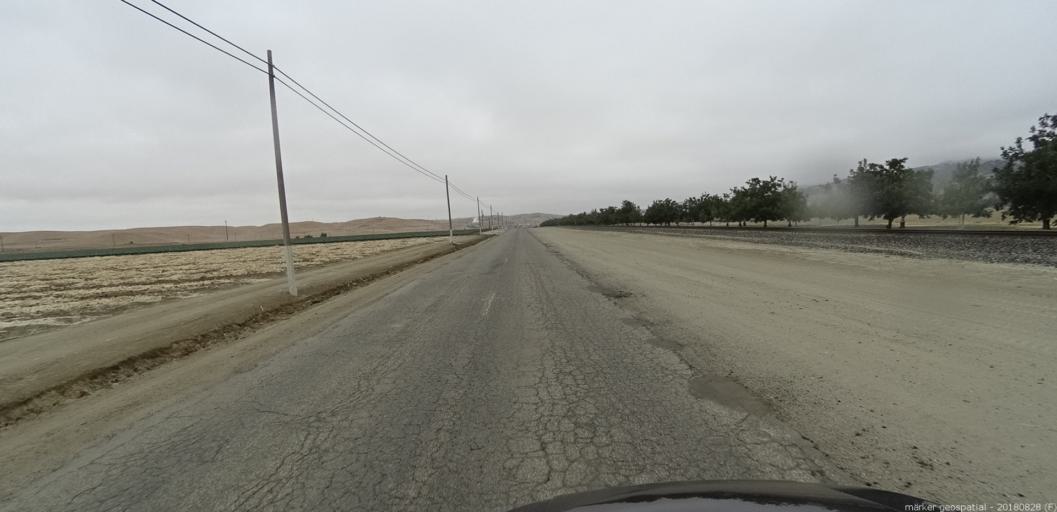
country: US
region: California
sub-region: San Luis Obispo County
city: Lake Nacimiento
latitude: 35.9764
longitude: -120.8771
